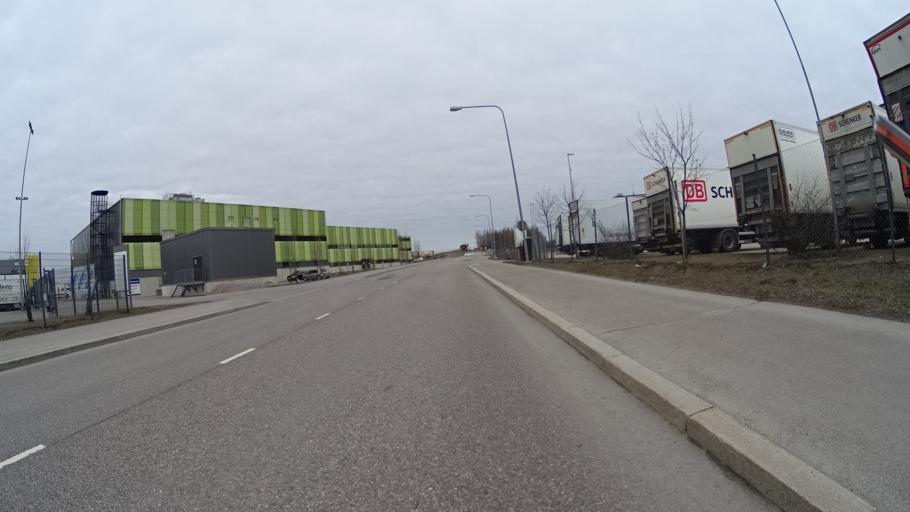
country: FI
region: Uusimaa
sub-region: Helsinki
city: Vantaa
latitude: 60.3017
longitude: 24.9126
